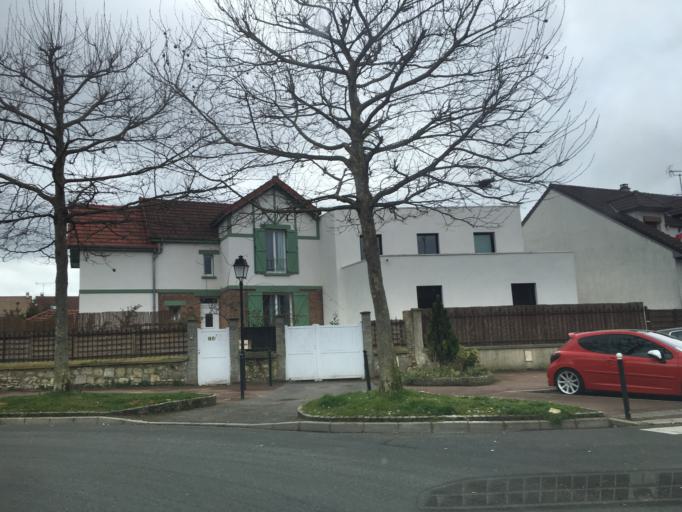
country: FR
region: Ile-de-France
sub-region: Departement du Val-de-Marne
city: Saint-Maur-des-Fosses
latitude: 48.7876
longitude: 2.4921
